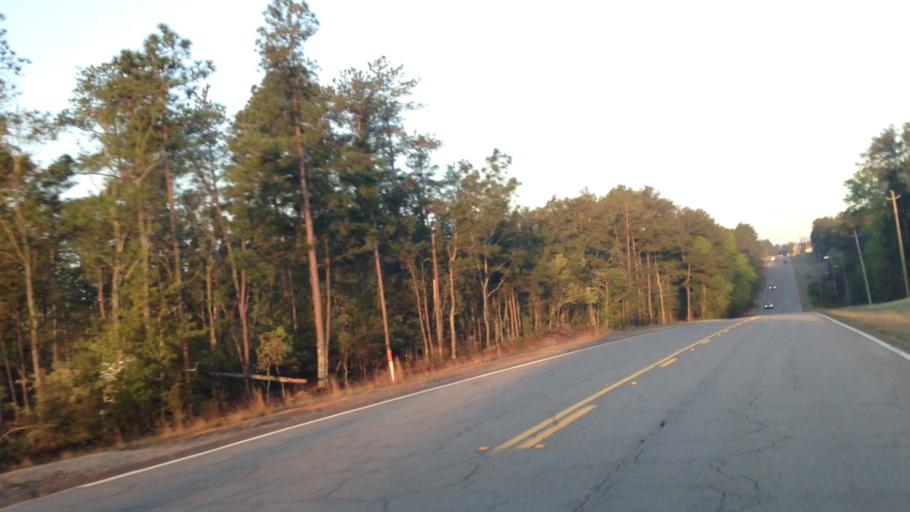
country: US
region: Georgia
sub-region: Columbia County
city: Grovetown
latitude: 33.4257
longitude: -82.1651
